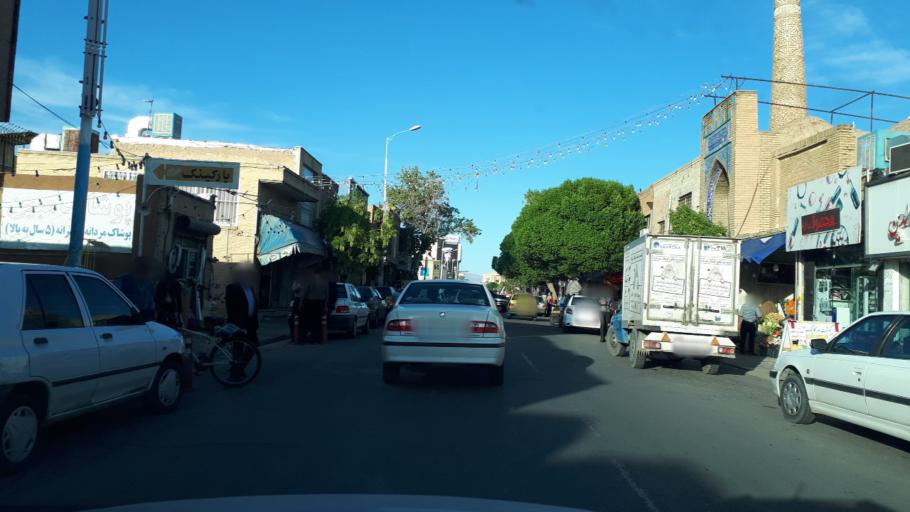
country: IR
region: Semnan
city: Semnan
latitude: 35.5666
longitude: 53.3989
